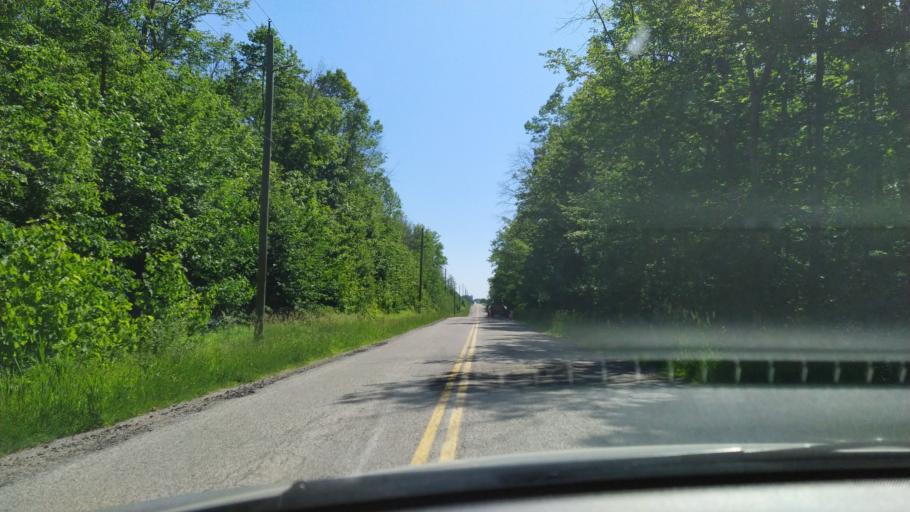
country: CA
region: Ontario
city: Waterloo
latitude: 43.4583
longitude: -80.7220
